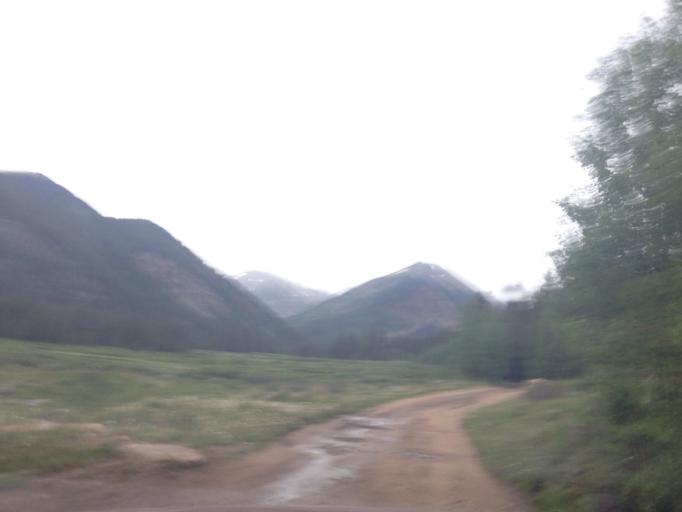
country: US
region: Colorado
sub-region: Clear Creek County
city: Georgetown
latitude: 39.5510
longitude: -105.7523
